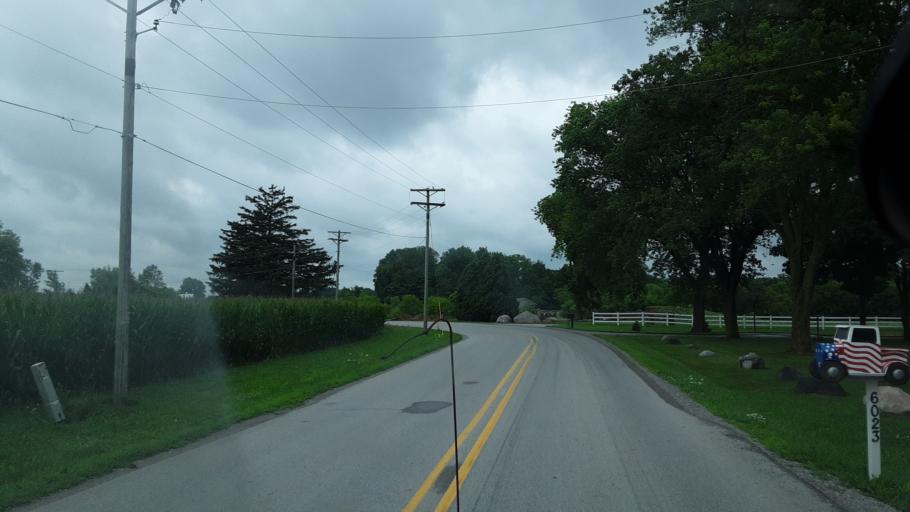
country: US
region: Indiana
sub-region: Wells County
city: Ossian
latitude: 40.9470
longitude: -85.0593
